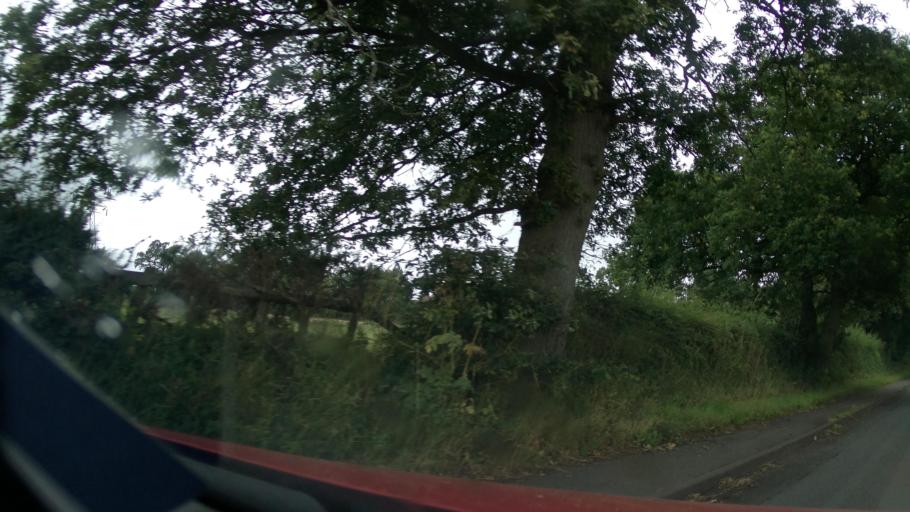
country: GB
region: England
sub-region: Solihull
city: Cheswick Green
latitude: 52.3834
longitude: -1.8221
